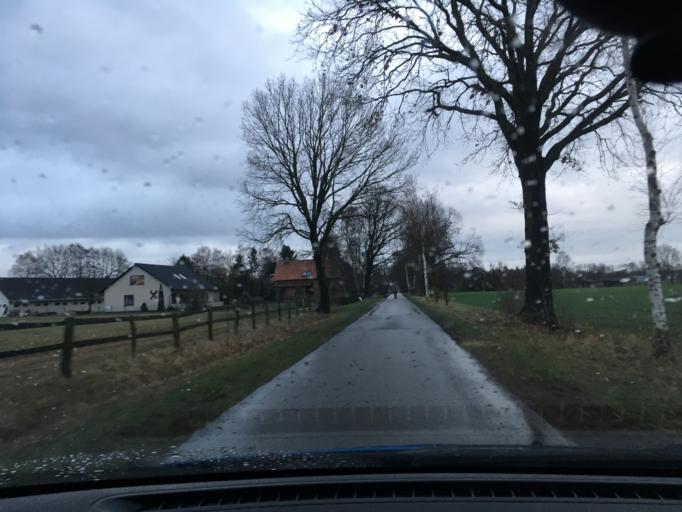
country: DE
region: Lower Saxony
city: Ludersburg
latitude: 53.3106
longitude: 10.6059
